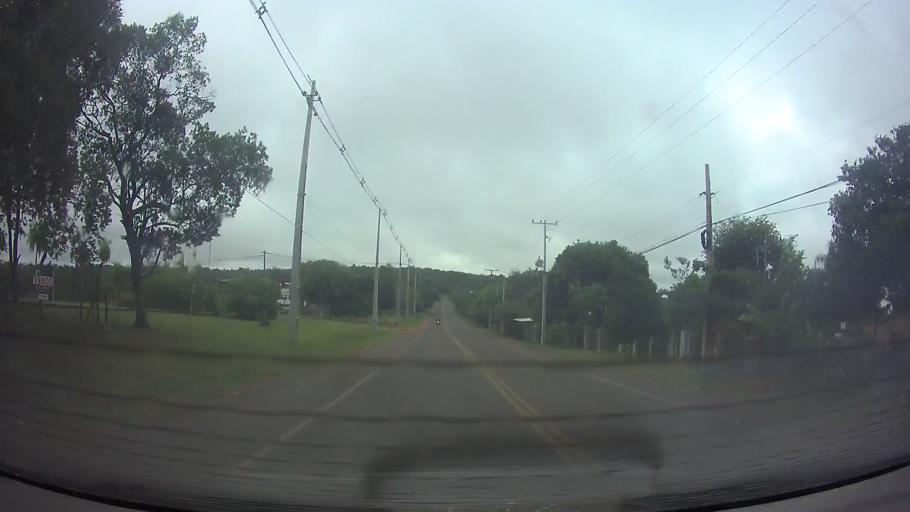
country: PY
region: Cordillera
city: Altos
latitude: -25.2889
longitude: -57.2668
